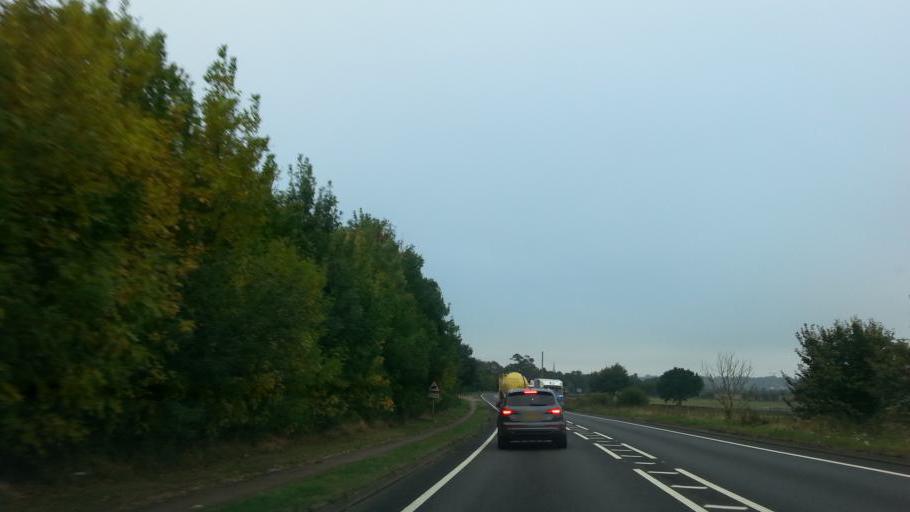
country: GB
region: England
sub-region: Northamptonshire
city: Oundle
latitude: 52.4978
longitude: -0.4462
